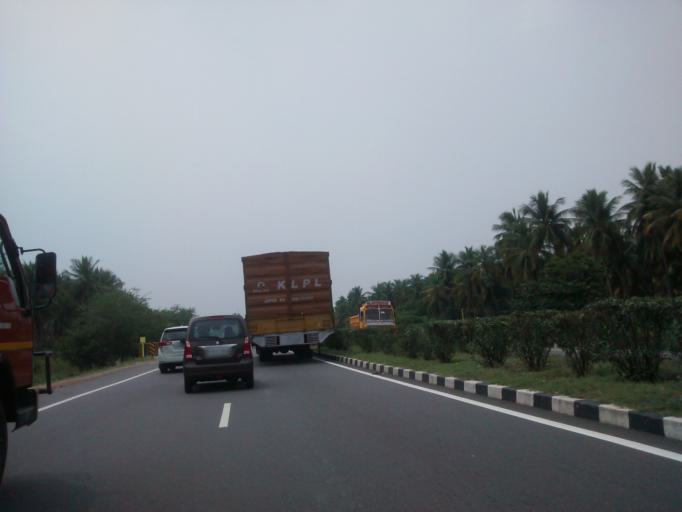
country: IN
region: Tamil Nadu
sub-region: Krishnagiri
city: Kaverippattanam
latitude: 12.2934
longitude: 78.2013
